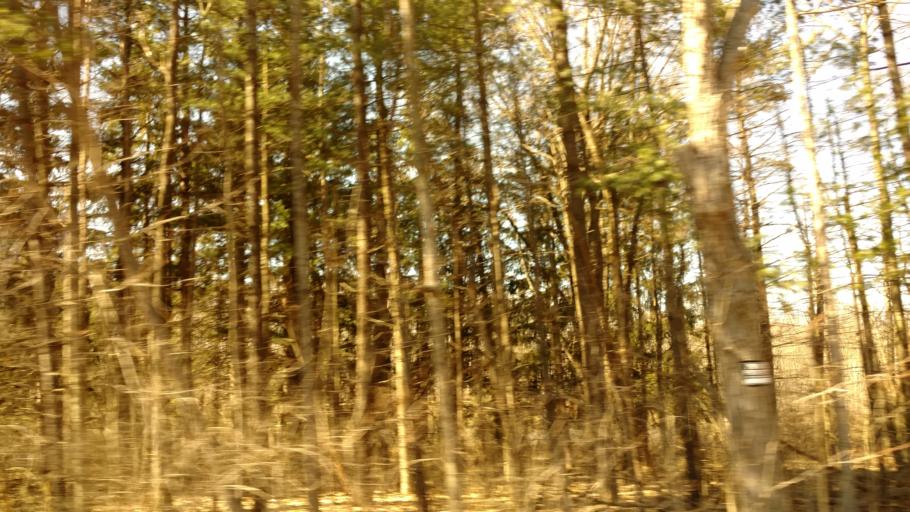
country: US
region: Ohio
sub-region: Marion County
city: Prospect
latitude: 40.5009
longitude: -83.1903
